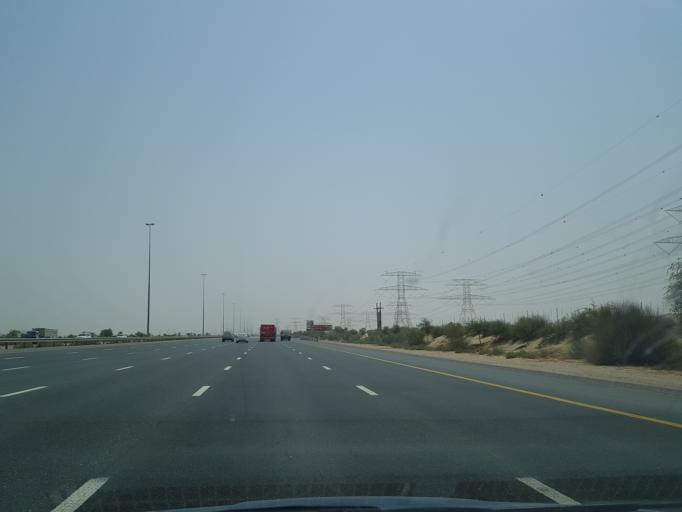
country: AE
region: Dubai
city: Dubai
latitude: 25.0652
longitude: 55.3396
